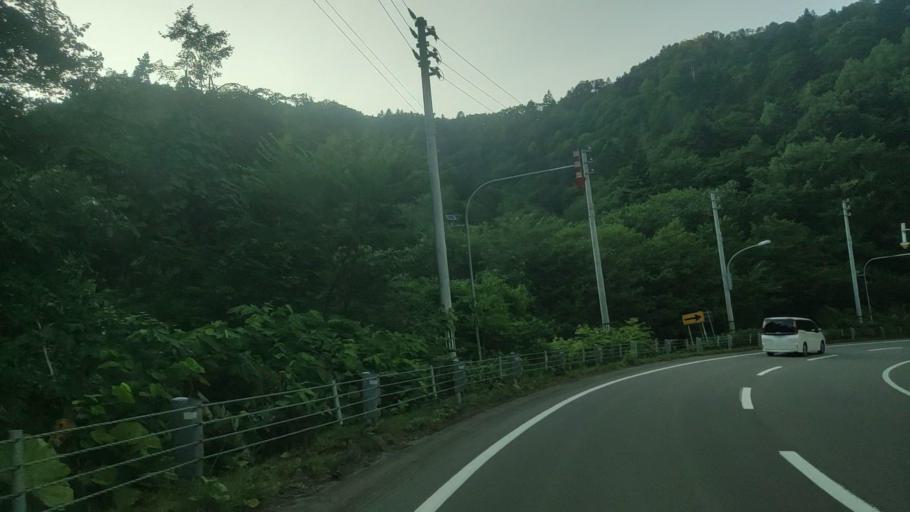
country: JP
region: Hokkaido
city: Bibai
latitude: 43.1810
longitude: 142.0638
